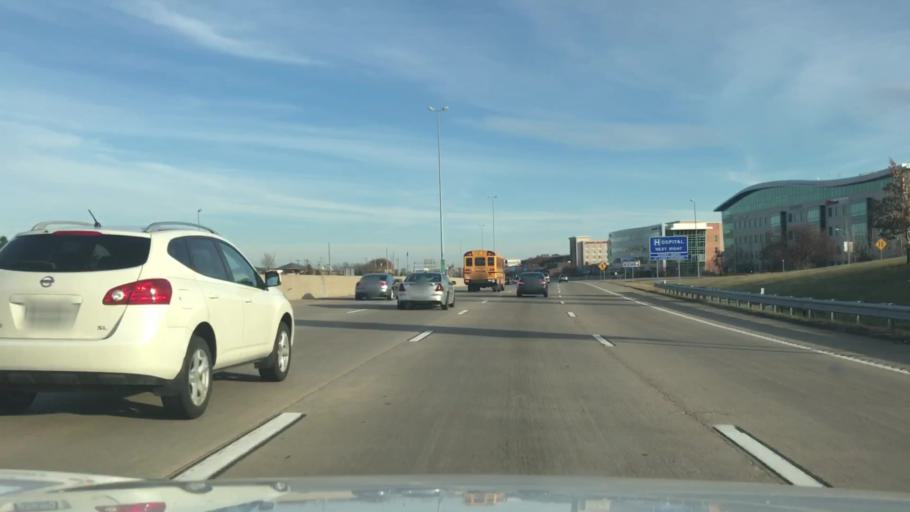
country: US
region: Missouri
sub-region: Saint Louis County
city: University City
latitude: 38.6317
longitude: -90.2854
